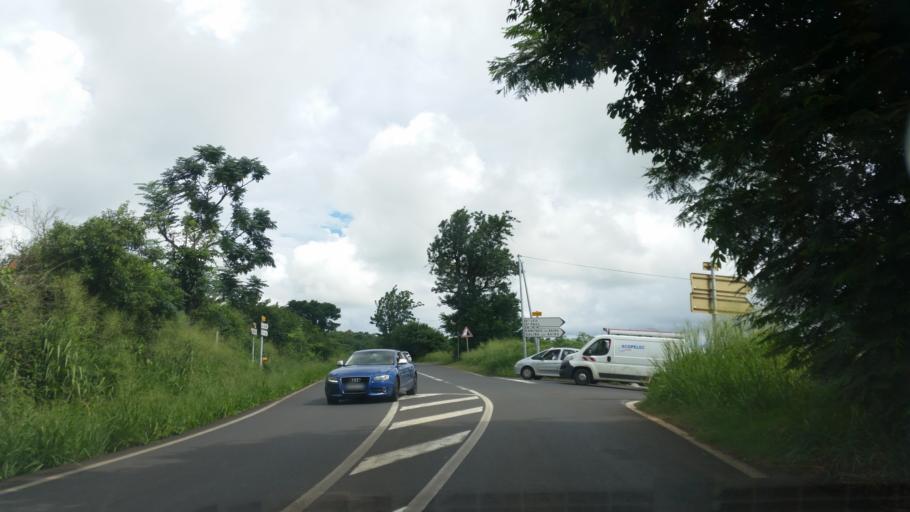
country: RE
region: Reunion
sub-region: Reunion
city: Trois-Bassins
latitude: -21.0647
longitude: 55.2670
